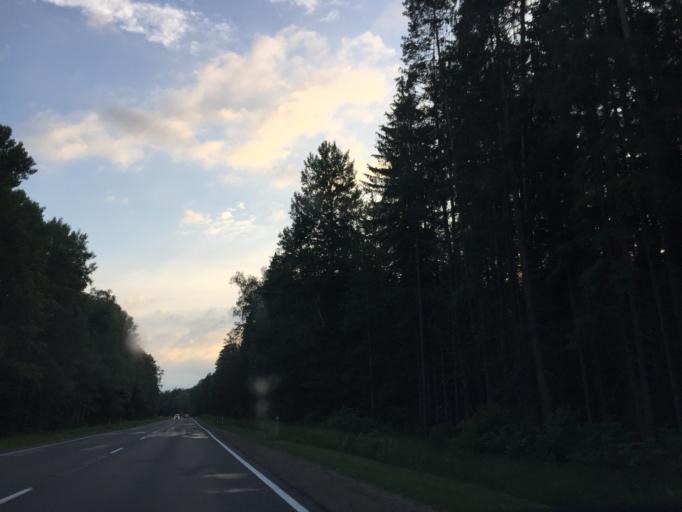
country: LV
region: Engure
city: Smarde
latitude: 56.9214
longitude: 23.4011
